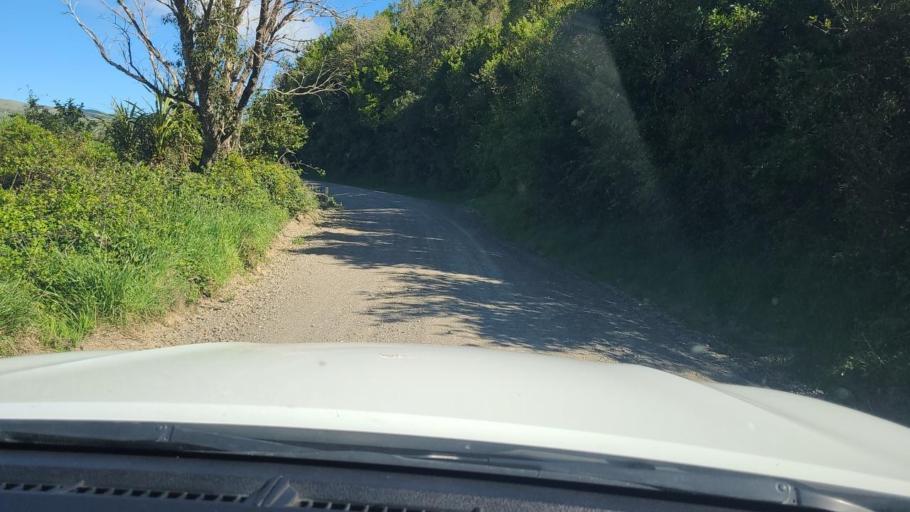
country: NZ
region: Hawke's Bay
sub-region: Napier City
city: Napier
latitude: -39.1447
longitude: 176.8223
